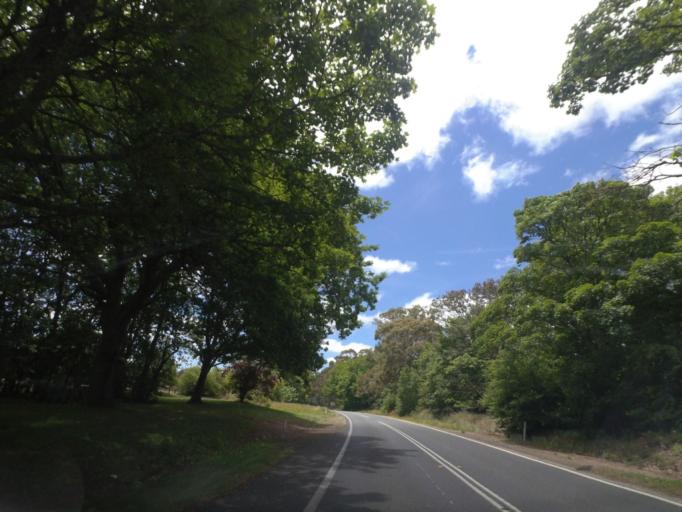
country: AU
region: Victoria
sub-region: Mount Alexander
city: Castlemaine
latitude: -37.3341
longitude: 144.1660
